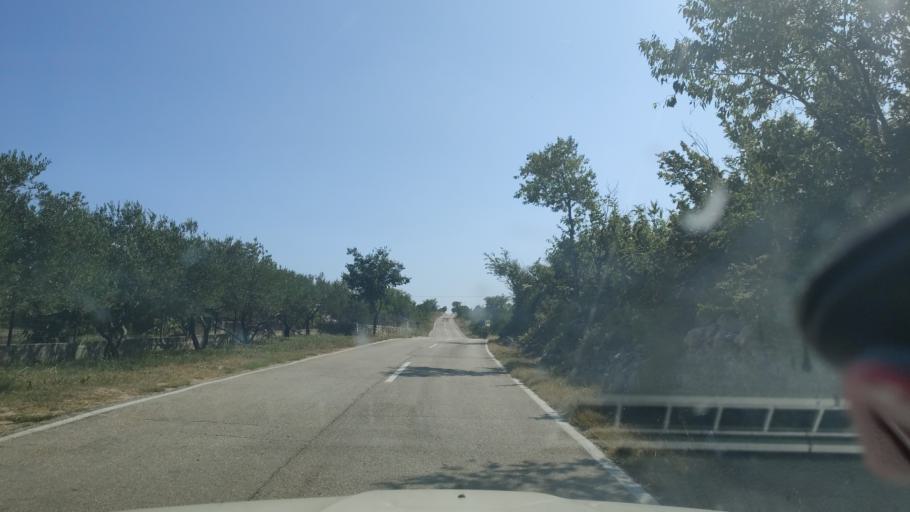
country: HR
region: Sibensko-Kniniska
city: Kistanje
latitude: 43.9129
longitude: 15.9436
